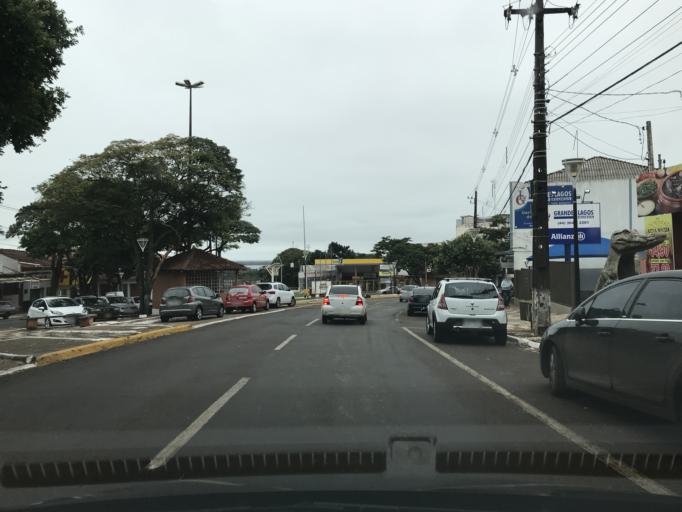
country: PY
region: Canindeyu
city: Salto del Guaira
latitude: -24.0814
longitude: -54.2548
